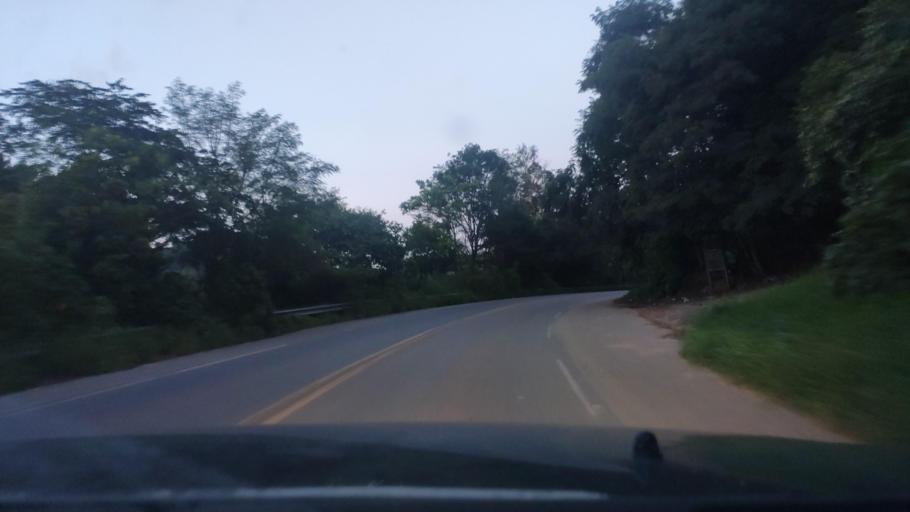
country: BR
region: Sao Paulo
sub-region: Campos Do Jordao
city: Campos do Jordao
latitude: -22.7523
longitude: -45.7434
